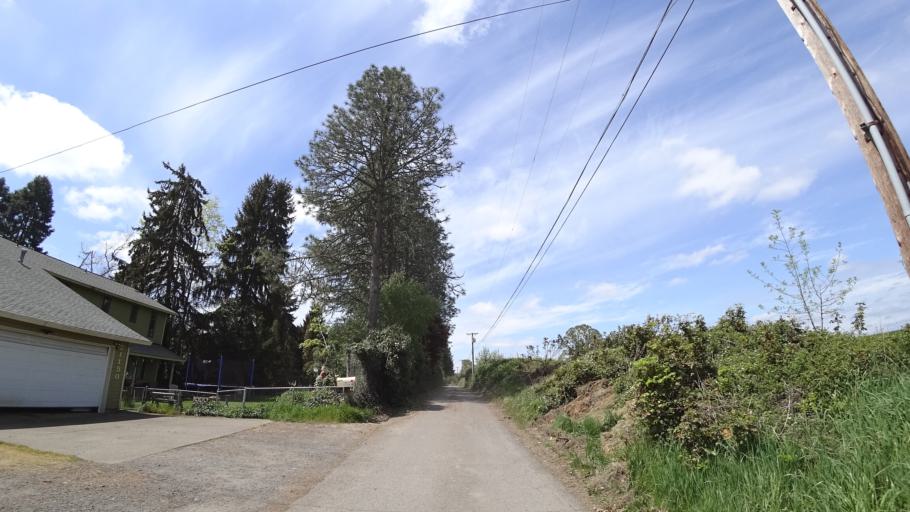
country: US
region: Oregon
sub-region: Washington County
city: Aloha
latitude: 45.4860
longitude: -122.8938
